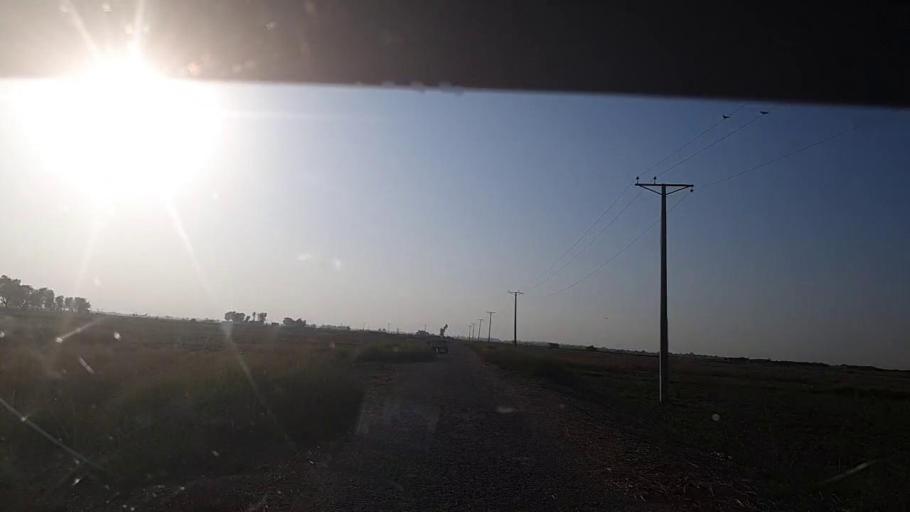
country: PK
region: Sindh
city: Ratodero
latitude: 27.8521
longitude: 68.2183
